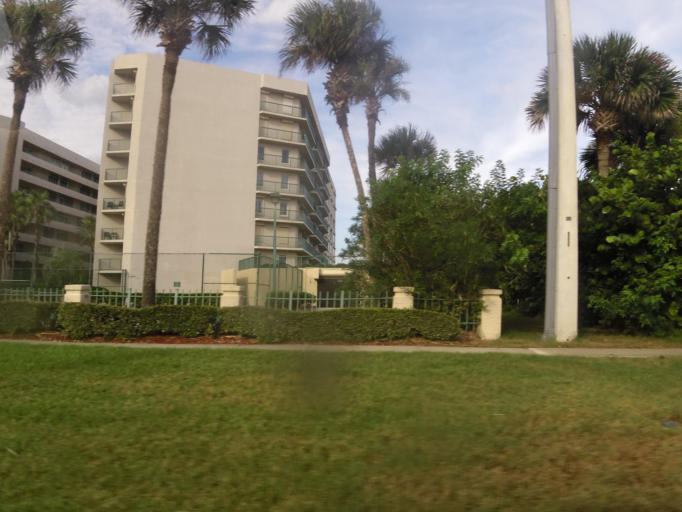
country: US
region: Florida
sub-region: Volusia County
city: Ponce Inlet
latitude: 29.1048
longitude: -80.9420
